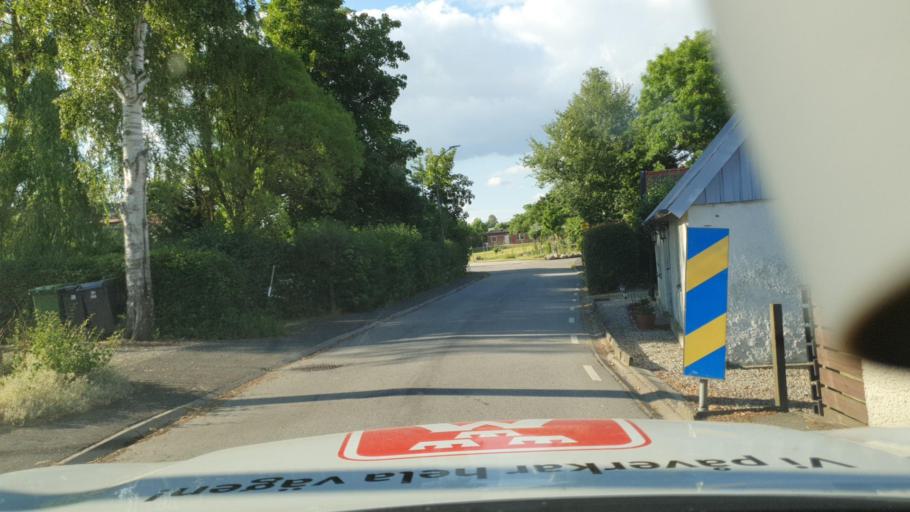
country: SE
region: Skane
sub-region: Skurups Kommun
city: Rydsgard
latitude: 55.5099
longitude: 13.5481
